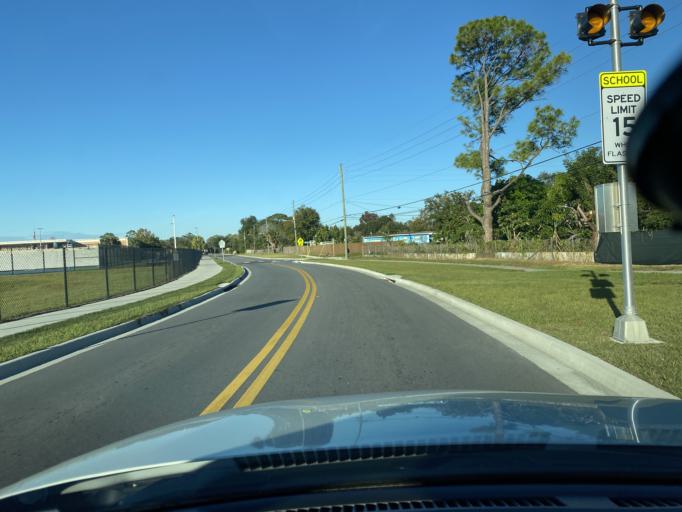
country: US
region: Florida
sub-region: Orange County
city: Azalea Park
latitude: 28.5317
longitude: -81.3011
